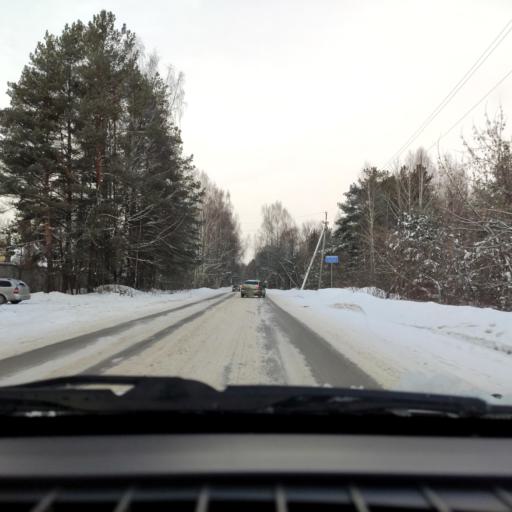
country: RU
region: Perm
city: Overyata
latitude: 58.0485
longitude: 55.8852
